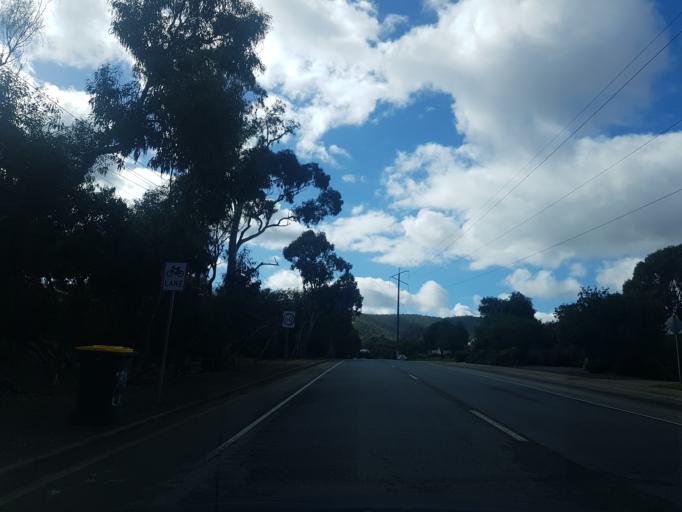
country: AU
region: South Australia
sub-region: Tea Tree Gully
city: Hope Valley
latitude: -34.8320
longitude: 138.7146
